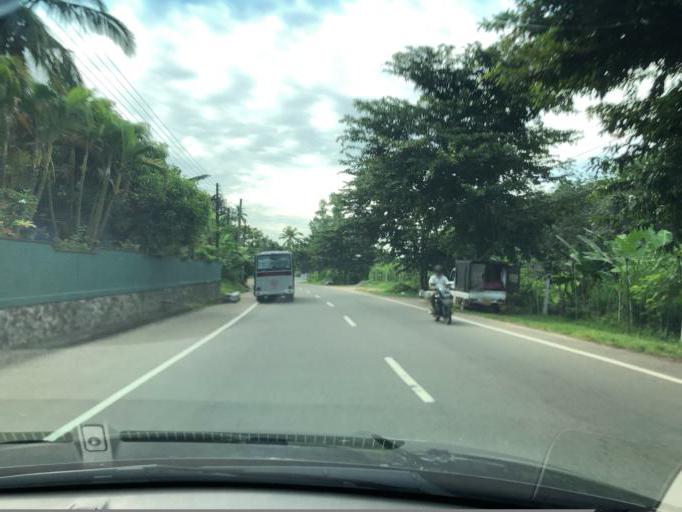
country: LK
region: Western
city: Kalutara
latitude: 6.5635
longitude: 80.0067
